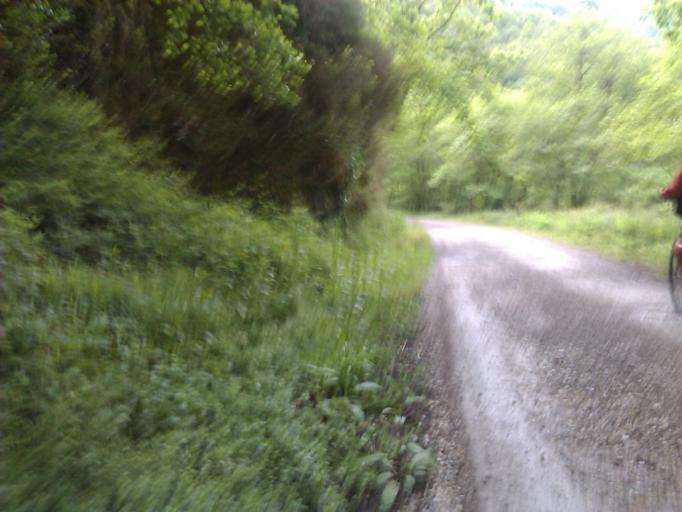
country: ES
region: Basque Country
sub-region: Provincia de Guipuzcoa
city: Elduayen
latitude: 43.1741
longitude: -1.9773
